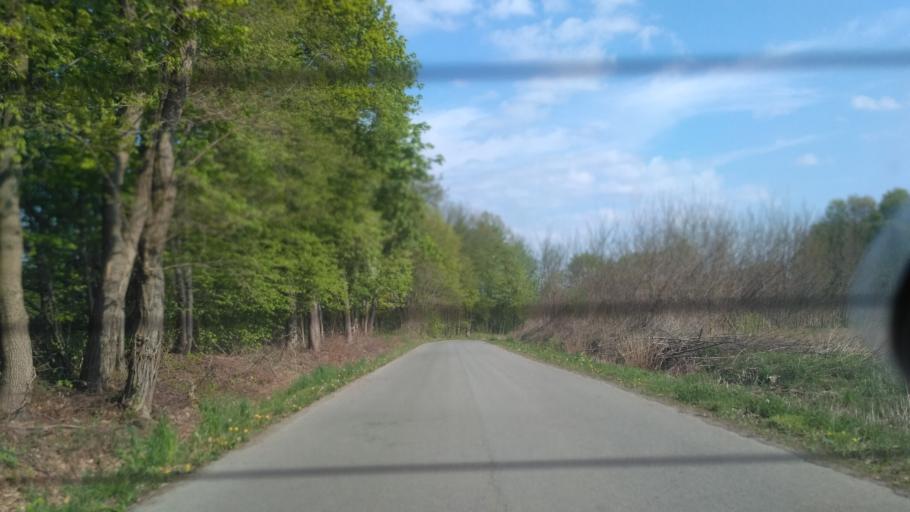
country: PL
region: Subcarpathian Voivodeship
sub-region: Powiat lubaczowski
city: Wielkie Oczy
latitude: 49.9723
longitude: 23.0605
